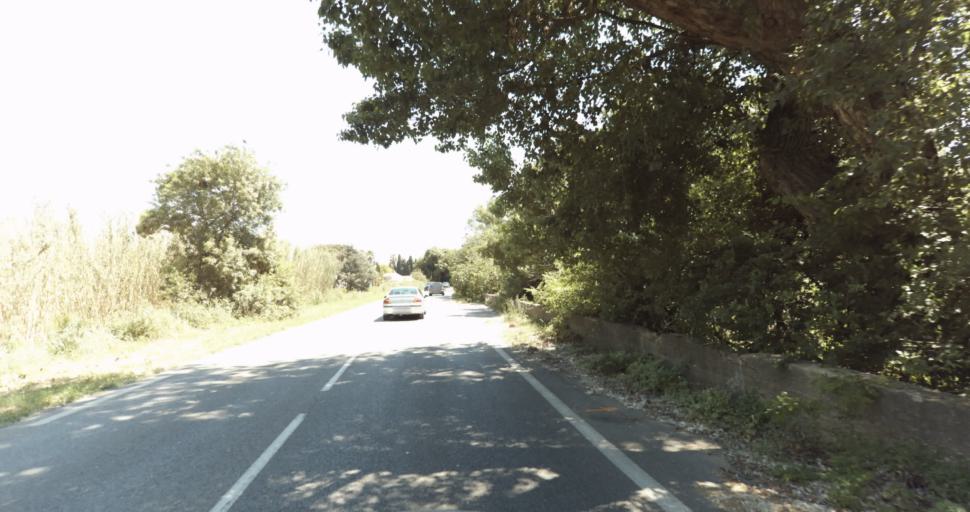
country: FR
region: Provence-Alpes-Cote d'Azur
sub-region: Departement du Var
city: Hyeres
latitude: 43.1335
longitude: 6.1618
